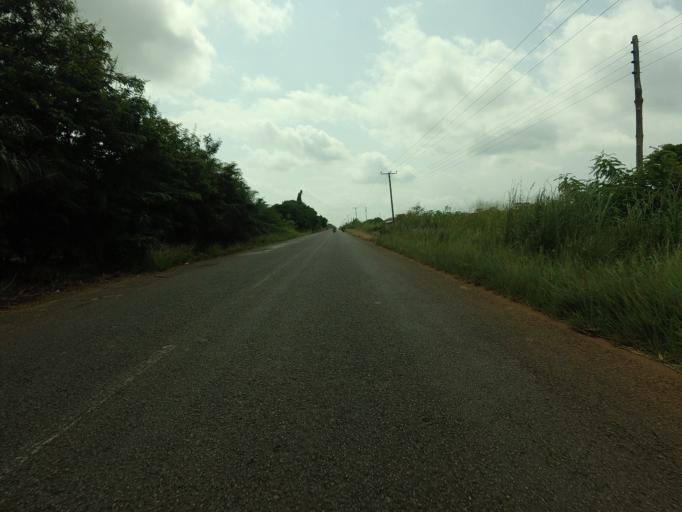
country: TG
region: Maritime
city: Lome
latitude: 6.1766
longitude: 1.0704
